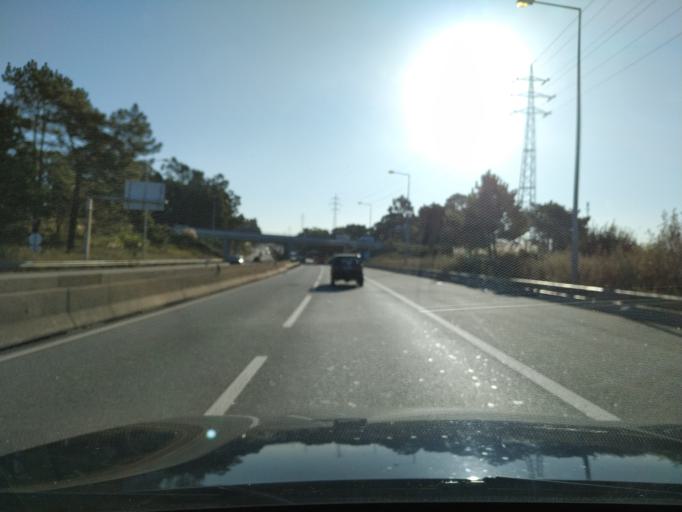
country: PT
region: Porto
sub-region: Vila Nova de Gaia
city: Vila Nova de Gaia
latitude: 41.1156
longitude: -8.6283
